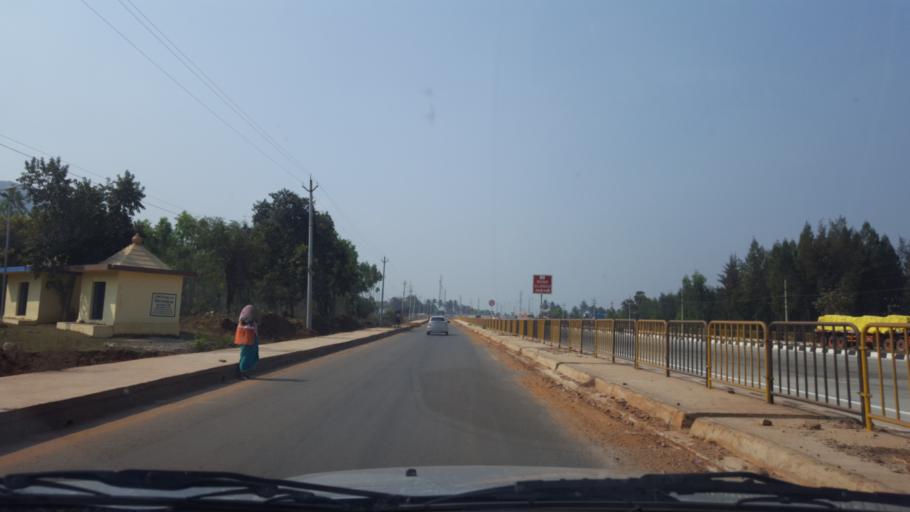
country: IN
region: Andhra Pradesh
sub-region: Vishakhapatnam
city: Vepagunta
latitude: 17.8526
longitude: 83.2737
